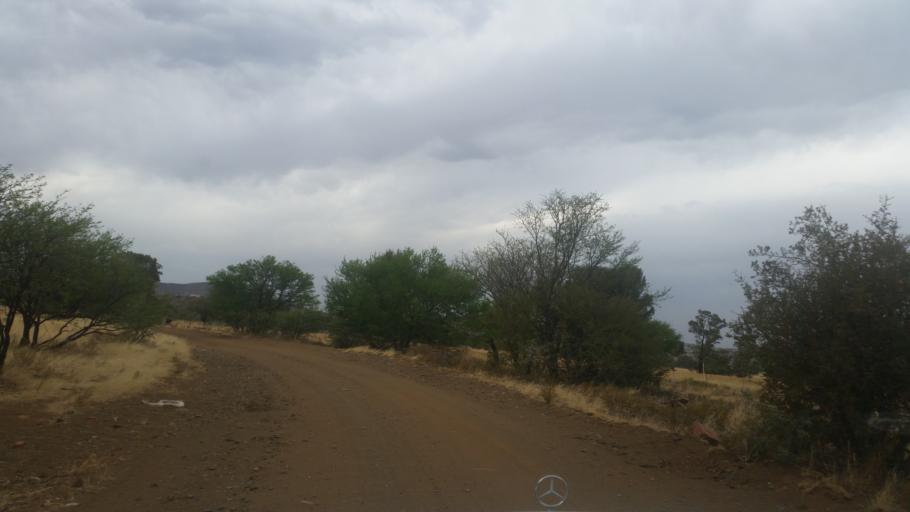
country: ZA
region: Orange Free State
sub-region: Xhariep District Municipality
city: Trompsburg
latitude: -30.5001
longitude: 25.9593
